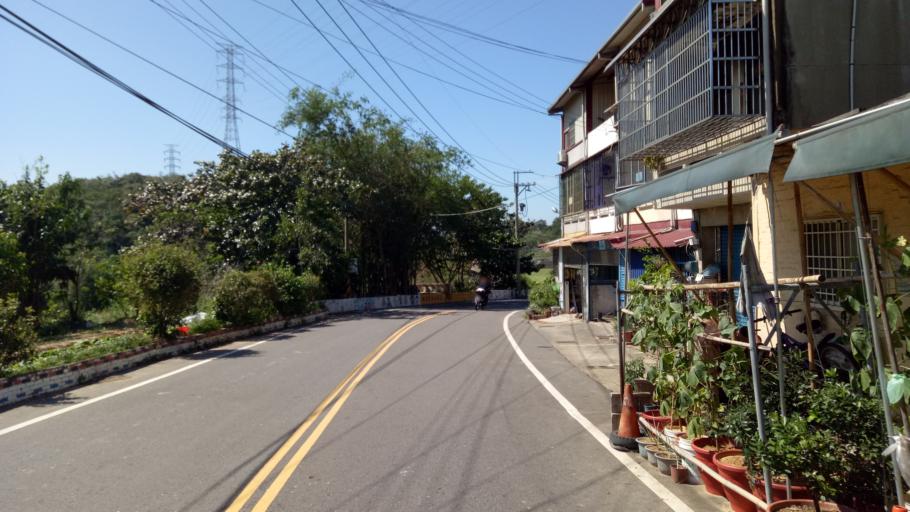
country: TW
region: Taiwan
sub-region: Hsinchu
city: Hsinchu
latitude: 24.7405
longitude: 120.9583
